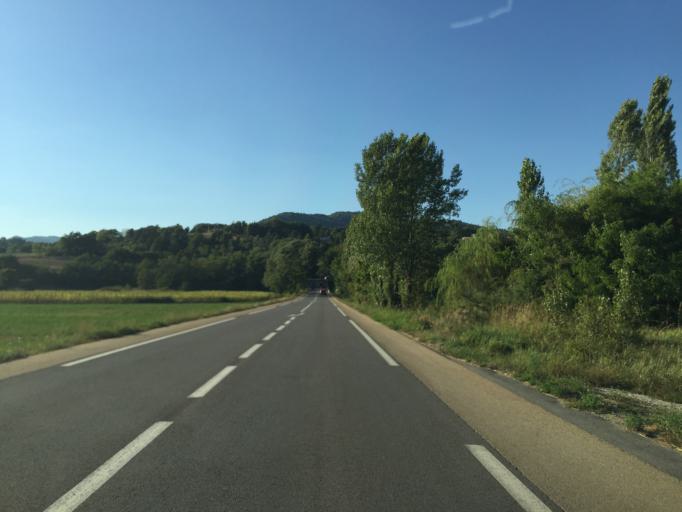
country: FR
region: Provence-Alpes-Cote d'Azur
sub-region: Departement des Alpes-de-Haute-Provence
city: Mallemoisson
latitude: 44.0444
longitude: 6.1387
